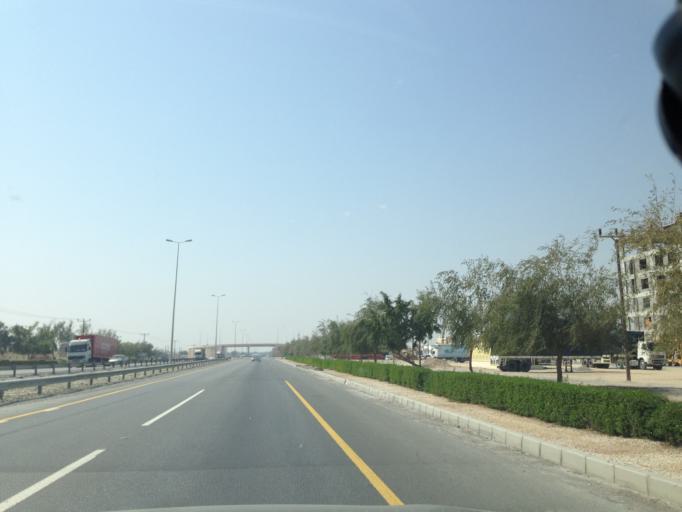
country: OM
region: Al Batinah
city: Barka'
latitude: 23.6646
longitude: 57.9531
